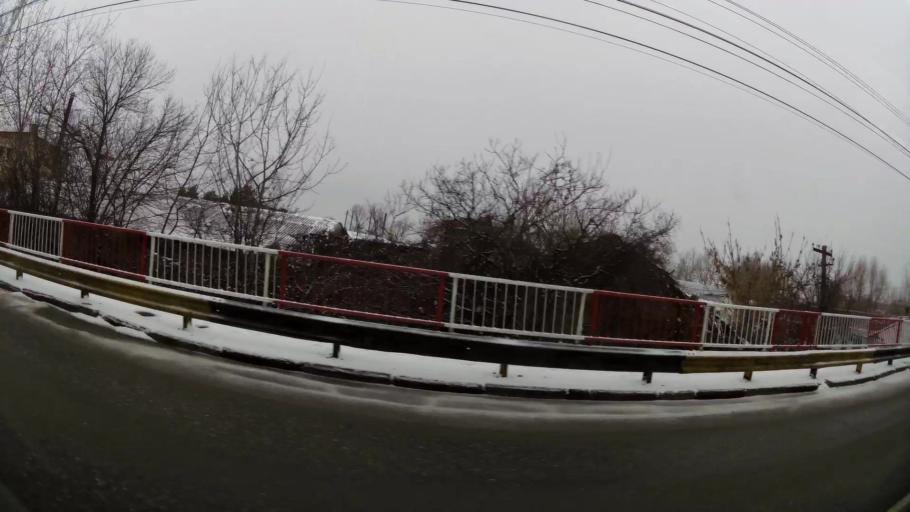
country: RO
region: Dambovita
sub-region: Municipiul Targoviste
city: Targoviste
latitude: 44.9156
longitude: 25.4515
